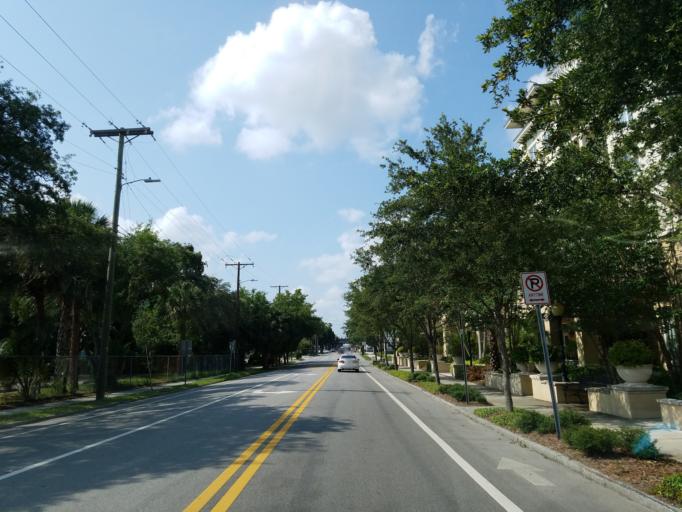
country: US
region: Florida
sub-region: Hillsborough County
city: Tampa
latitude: 27.9402
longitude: -82.4686
